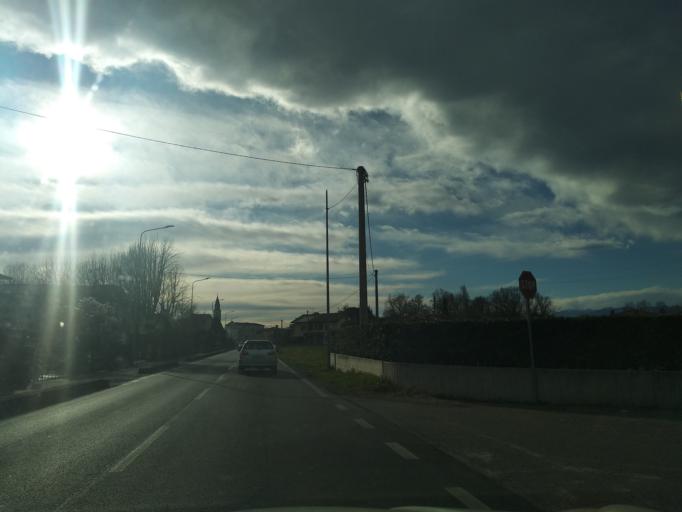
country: IT
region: Veneto
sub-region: Provincia di Vicenza
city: Bressanvido
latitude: 45.6489
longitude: 11.6393
